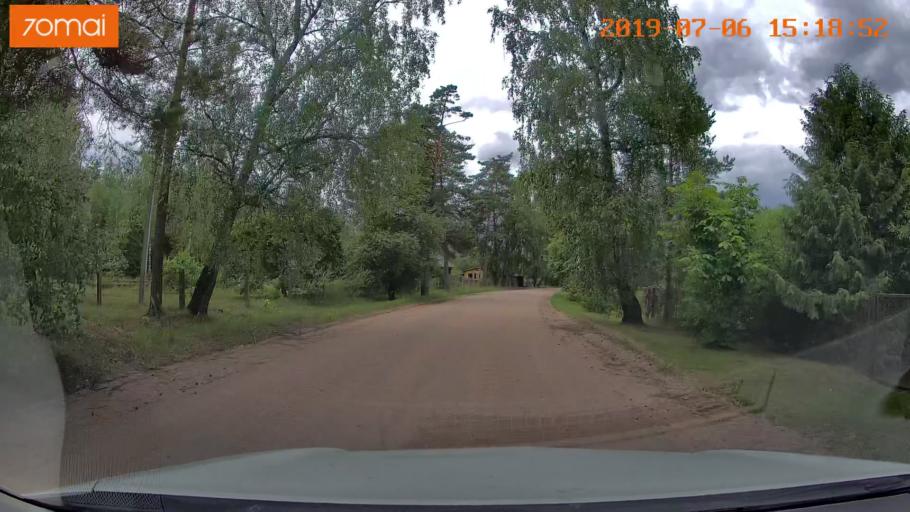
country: BY
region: Minsk
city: Ivyanyets
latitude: 53.9938
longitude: 26.6497
